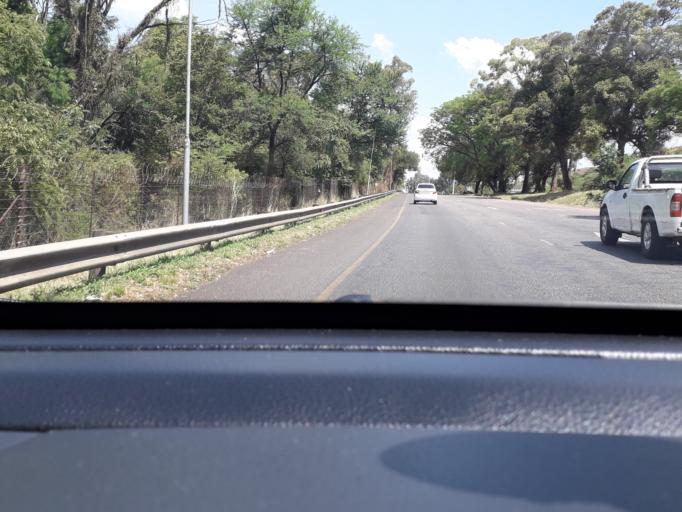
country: ZA
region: Gauteng
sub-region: City of Tshwane Metropolitan Municipality
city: Pretoria
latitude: -25.7825
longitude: 28.1935
